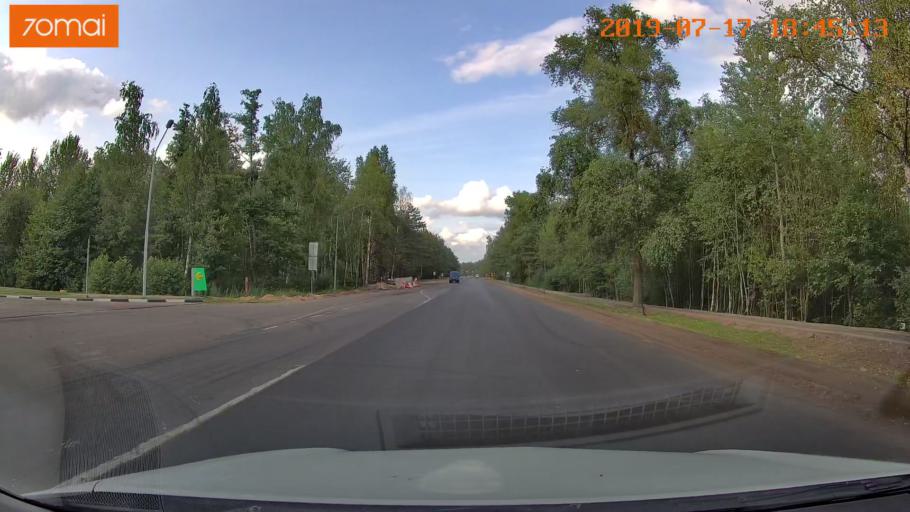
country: BY
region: Mogilev
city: Asipovichy
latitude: 53.3232
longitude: 28.6524
